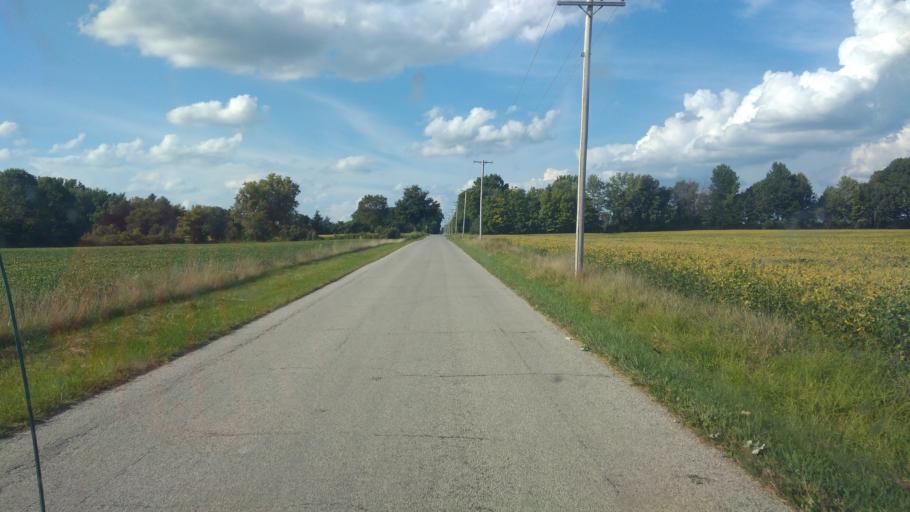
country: US
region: Ohio
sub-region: Crawford County
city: Galion
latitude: 40.7464
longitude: -82.7745
